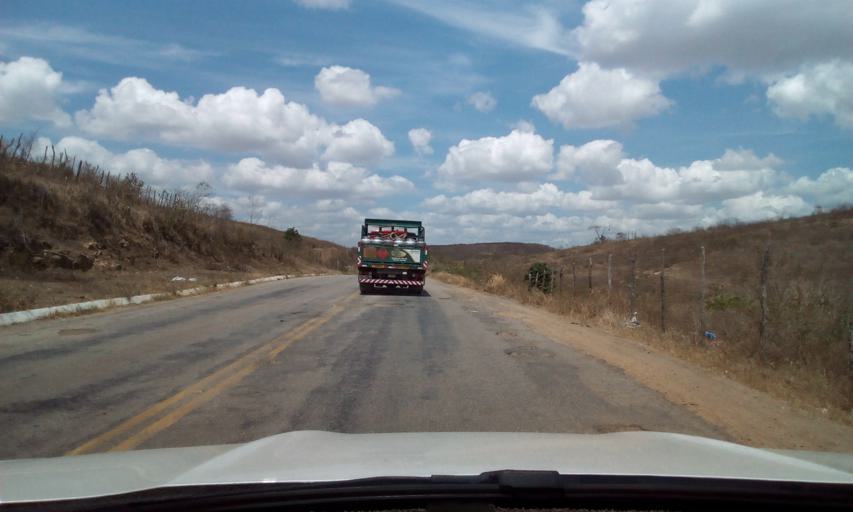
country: BR
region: Paraiba
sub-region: Gurinhem
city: Gurinhem
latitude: -7.1183
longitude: -35.4299
